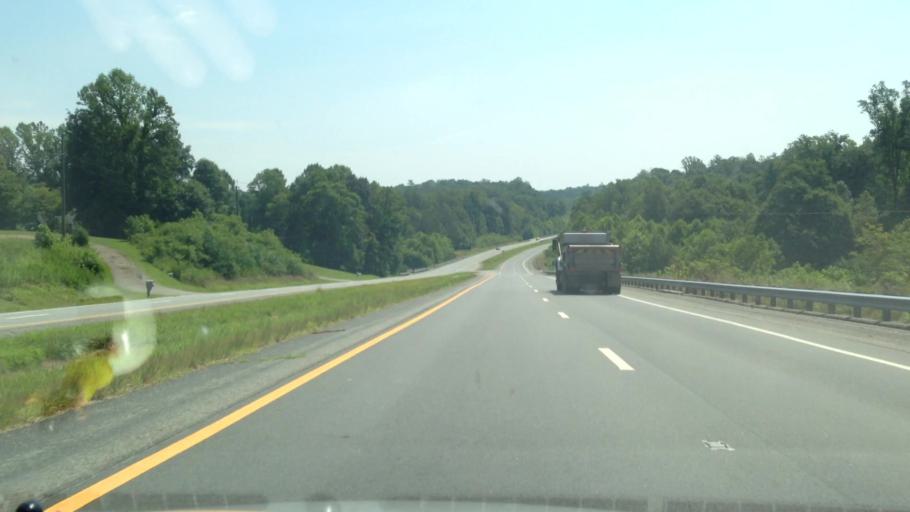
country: US
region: Virginia
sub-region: Patrick County
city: Patrick Springs
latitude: 36.5900
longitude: -80.1236
